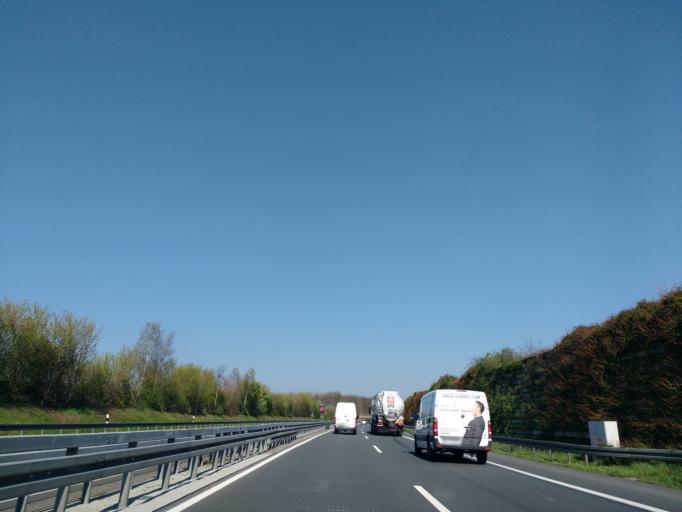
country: DE
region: Lower Saxony
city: Dissen
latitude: 52.1074
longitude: 8.1849
